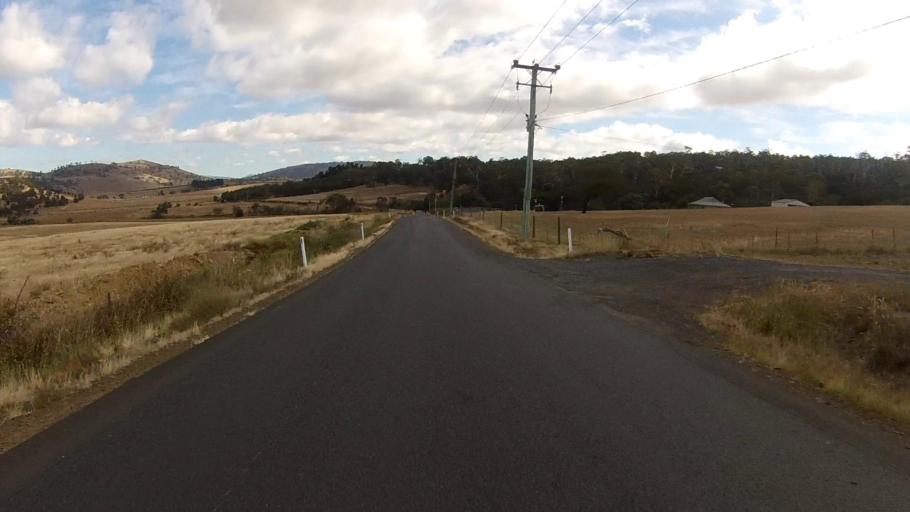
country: AU
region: Tasmania
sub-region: Brighton
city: Old Beach
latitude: -42.7559
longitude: 147.3050
